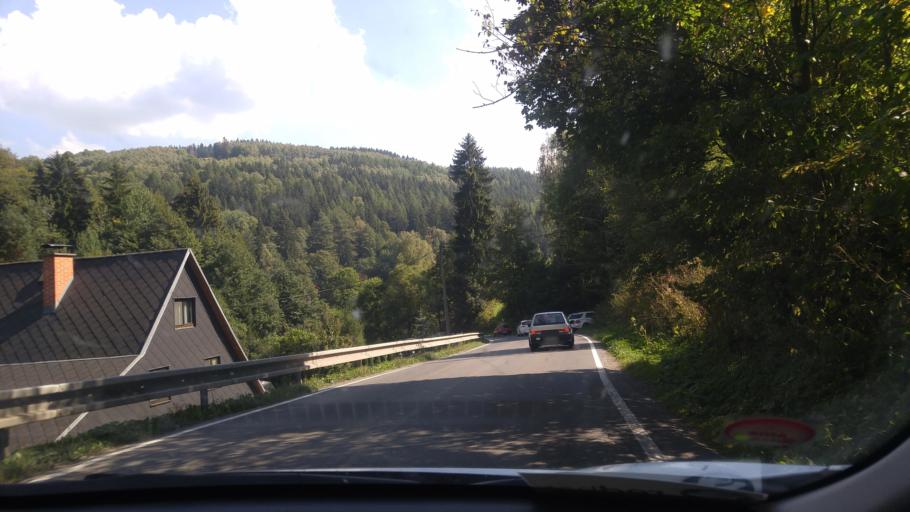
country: CZ
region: Olomoucky
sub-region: Okres Sumperk
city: Stare Mesto
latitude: 50.1495
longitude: 17.0111
